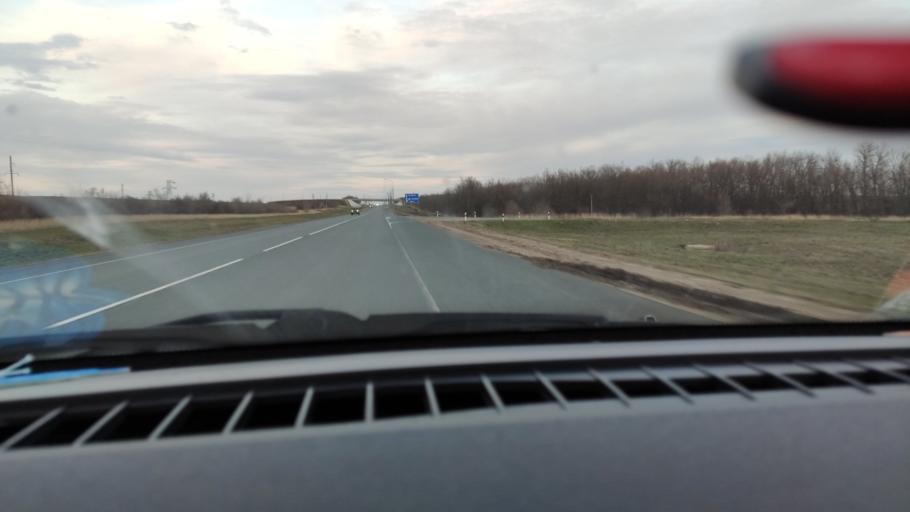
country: RU
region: Saratov
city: Yelshanka
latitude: 51.8253
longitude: 46.2915
